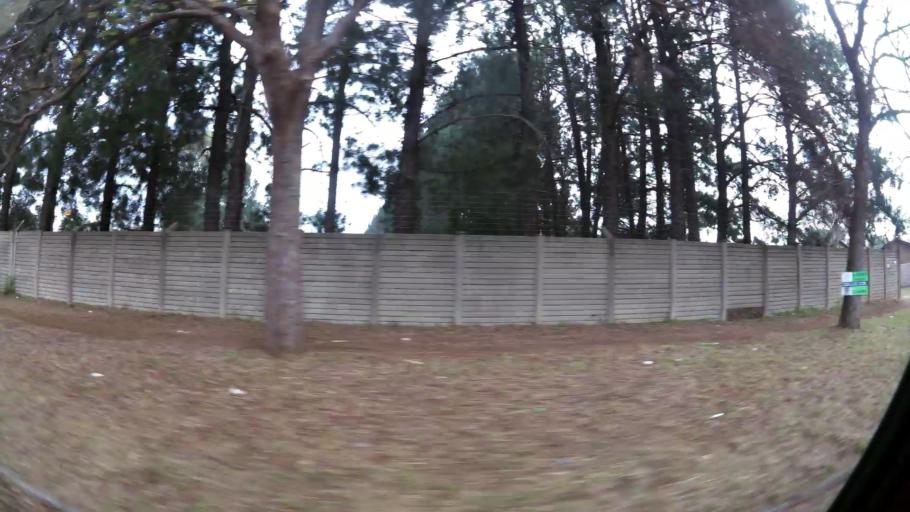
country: ZA
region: Gauteng
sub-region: Sedibeng District Municipality
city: Vanderbijlpark
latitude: -26.6869
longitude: 27.8271
